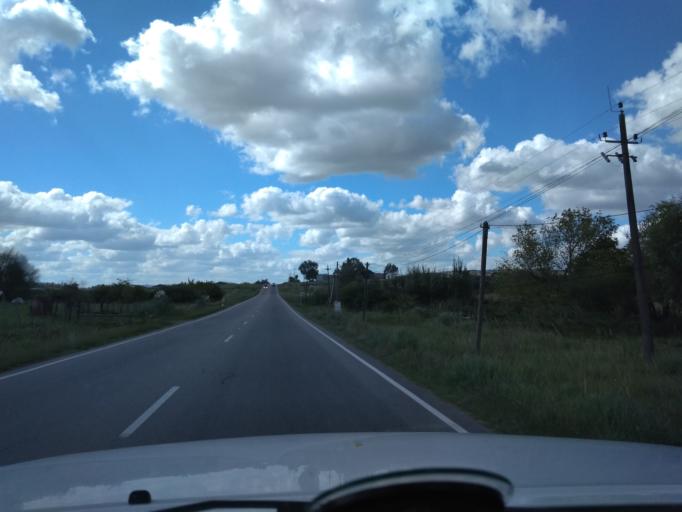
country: UY
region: Canelones
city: Joaquin Suarez
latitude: -34.7059
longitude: -56.0582
